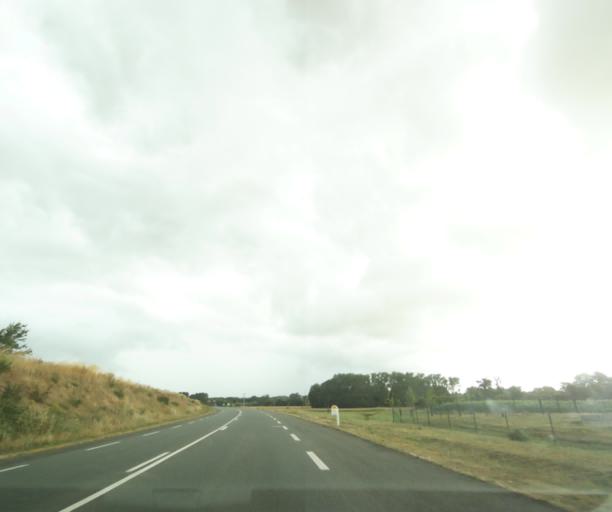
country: FR
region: Pays de la Loire
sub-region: Departement de la Vendee
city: Saint-Hilaire-de-Talmont
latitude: 46.4609
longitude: -1.6042
